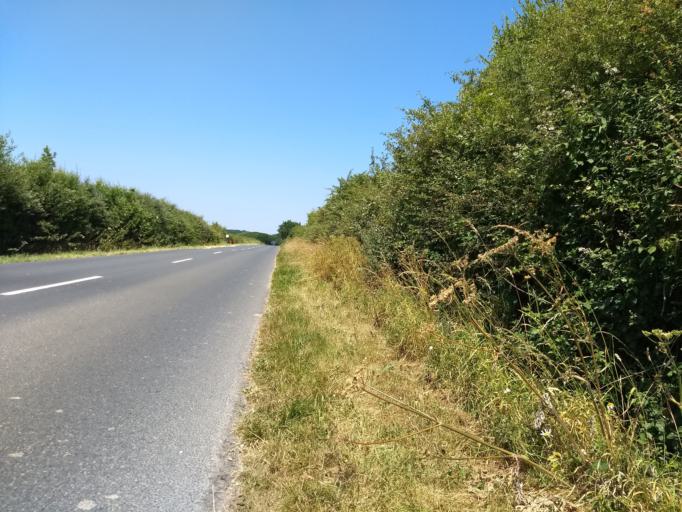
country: GB
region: England
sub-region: Isle of Wight
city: Northwood
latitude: 50.7059
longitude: -1.3470
